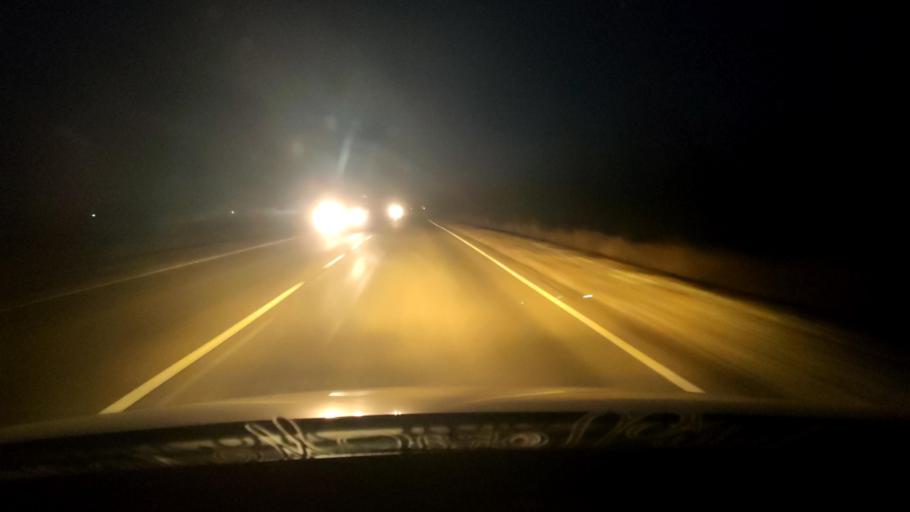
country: RU
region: Voronezj
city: Podgornoye
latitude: 51.8680
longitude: 39.0962
